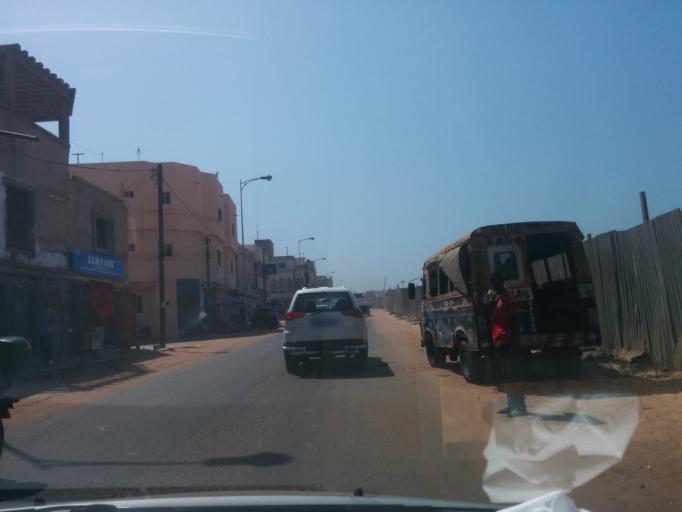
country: SN
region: Dakar
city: Grand Dakar
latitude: 14.7578
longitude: -17.4523
